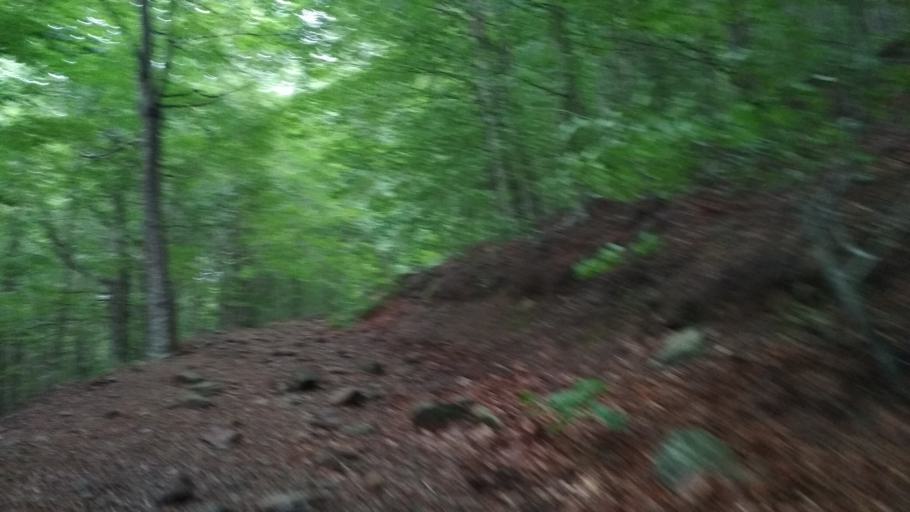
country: ES
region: Catalonia
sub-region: Provincia de Barcelona
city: Fogars de Montclus
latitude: 41.7786
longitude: 2.4492
